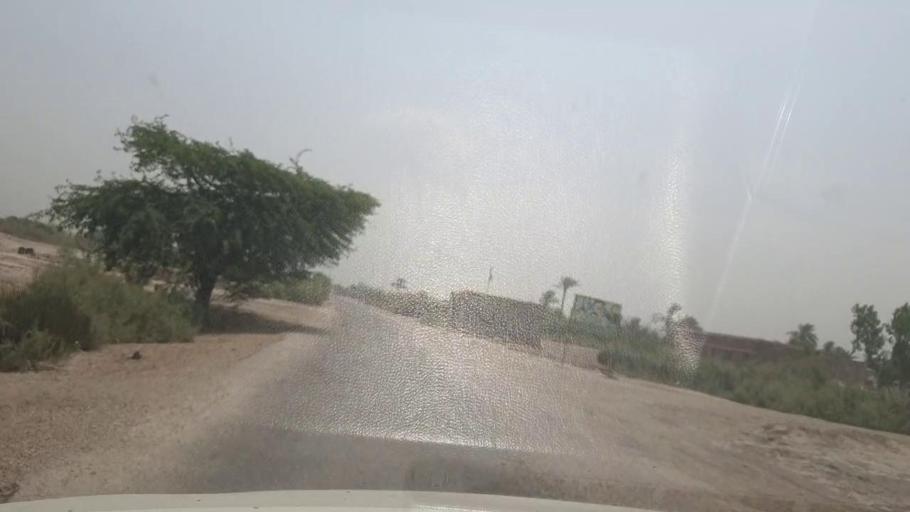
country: PK
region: Sindh
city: Kot Diji
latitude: 27.3758
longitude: 68.7028
